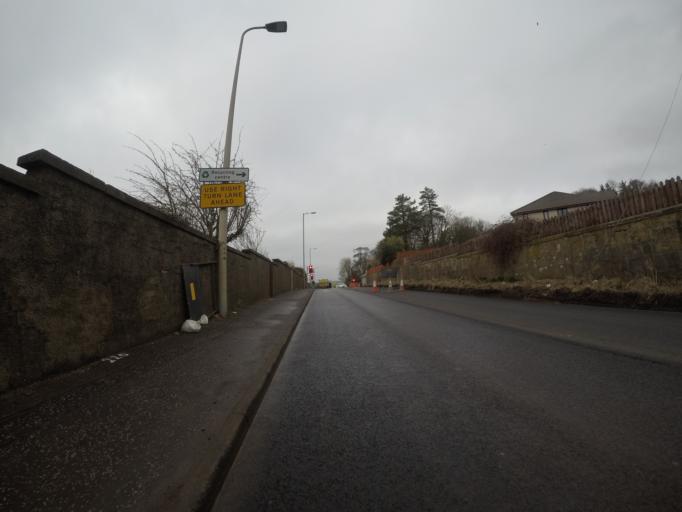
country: GB
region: Scotland
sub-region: North Ayrshire
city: Largs
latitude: 55.7845
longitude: -4.8577
